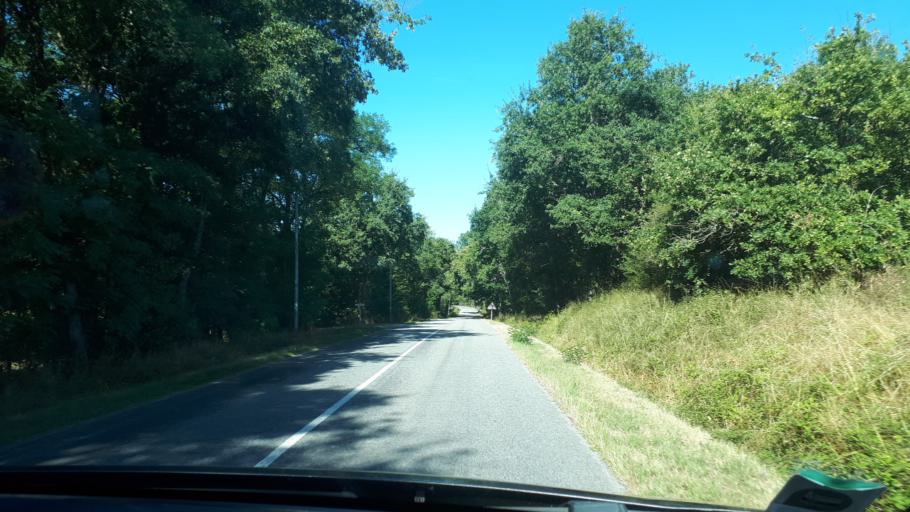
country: FR
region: Centre
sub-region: Departement du Loiret
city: Saint-Brisson-sur-Loire
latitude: 47.5958
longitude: 2.6908
